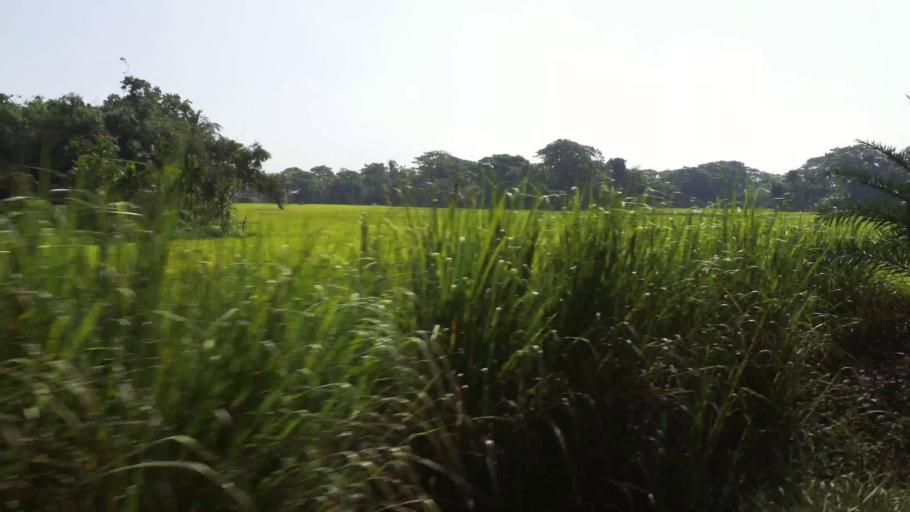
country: BD
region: Dhaka
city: Gafargaon
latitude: 24.5051
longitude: 90.5179
